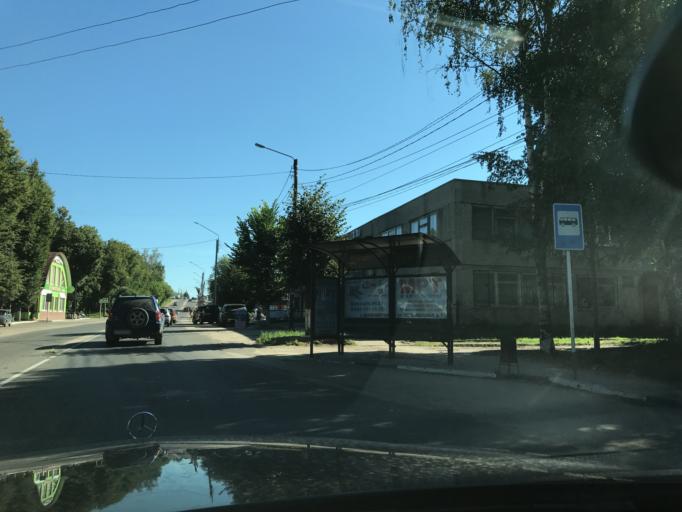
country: RU
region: Vladimir
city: Kirzhach
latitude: 56.1588
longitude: 38.8666
